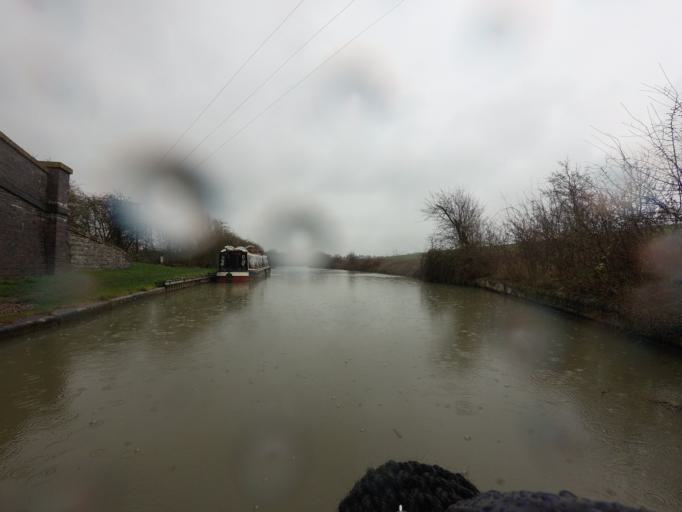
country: GB
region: England
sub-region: Northamptonshire
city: Blisworth
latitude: 52.1816
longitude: -0.9427
